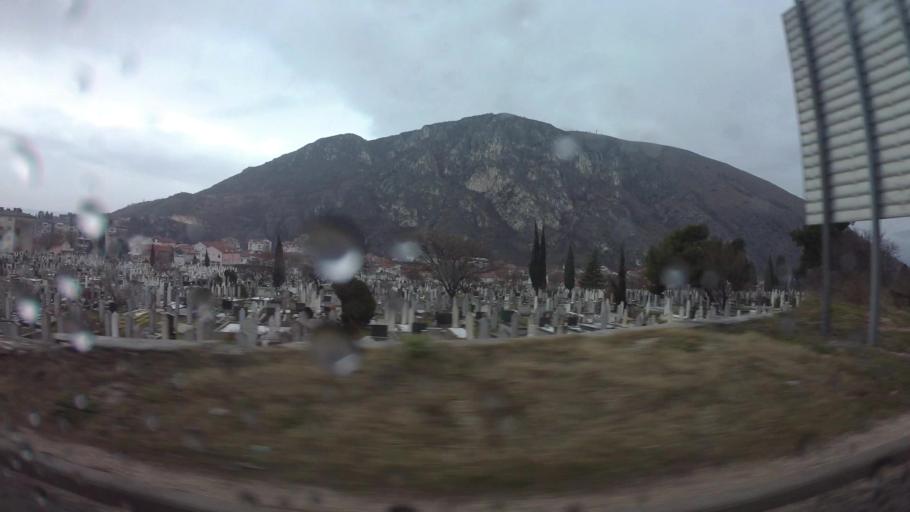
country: BA
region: Federation of Bosnia and Herzegovina
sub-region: Hercegovacko-Bosanski Kanton
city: Mostar
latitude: 43.3304
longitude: 17.8214
